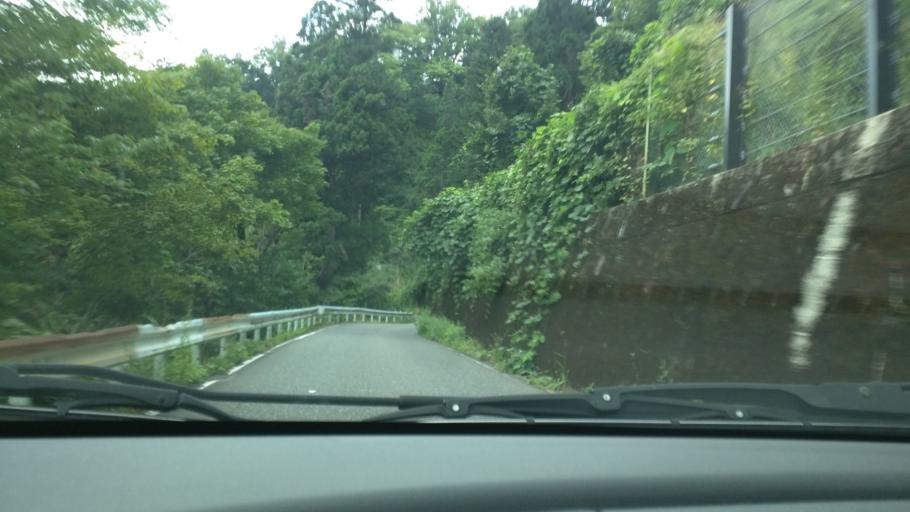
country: JP
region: Fukushima
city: Kitakata
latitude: 37.4616
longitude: 139.6459
